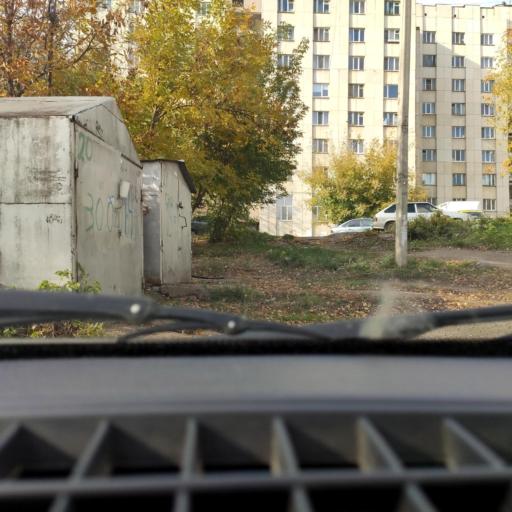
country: RU
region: Bashkortostan
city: Ufa
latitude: 54.7351
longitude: 55.9900
